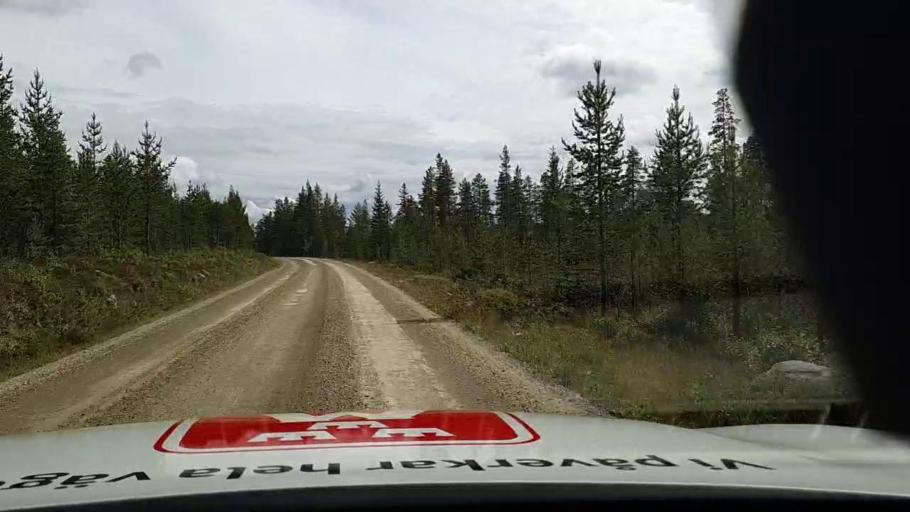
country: SE
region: Jaemtland
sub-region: Are Kommun
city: Jarpen
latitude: 62.5367
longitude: 13.4769
